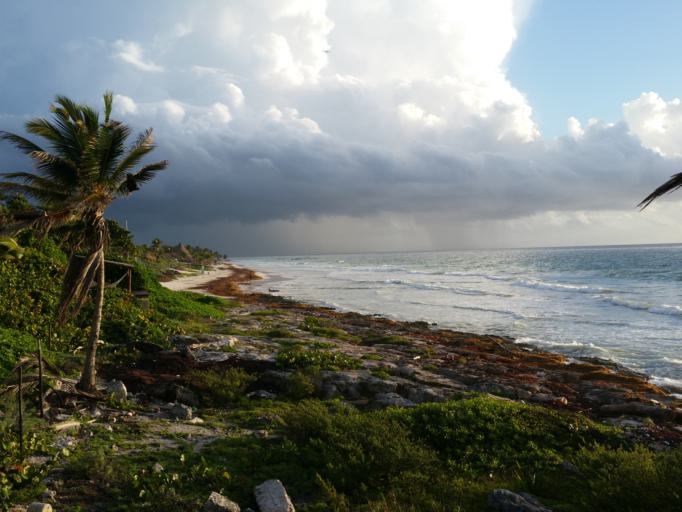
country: MX
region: Quintana Roo
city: Tulum
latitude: 20.1967
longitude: -87.4377
